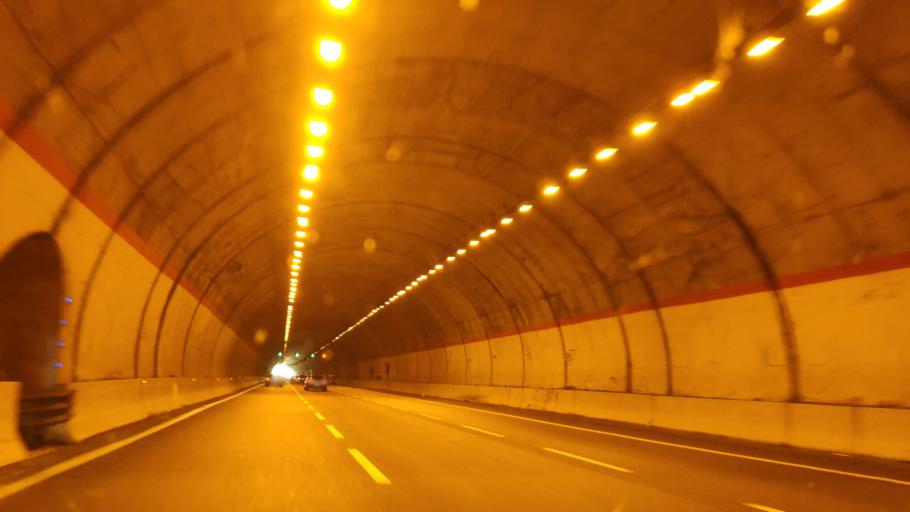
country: IT
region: Campania
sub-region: Provincia di Salerno
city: Piegolelle-San Bartolomeo
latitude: 40.6989
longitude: 14.8173
